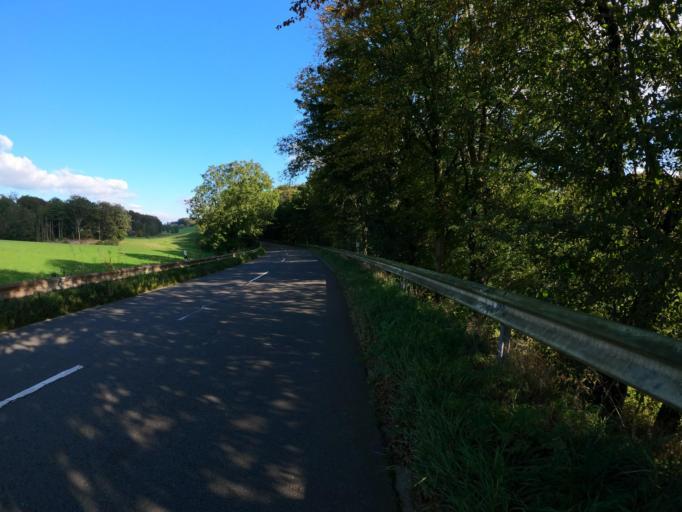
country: DE
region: North Rhine-Westphalia
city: Radevormwald
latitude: 51.2267
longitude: 7.3450
